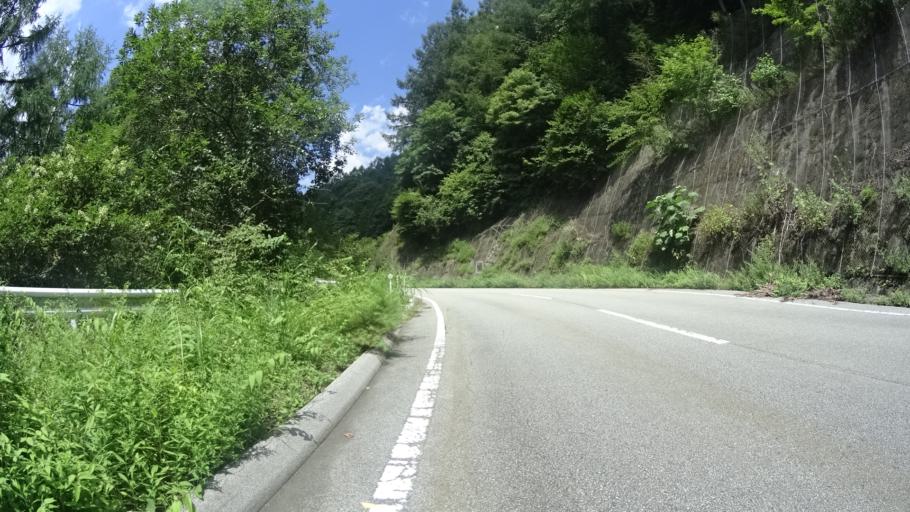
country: JP
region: Yamanashi
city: Enzan
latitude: 35.7975
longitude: 138.6767
